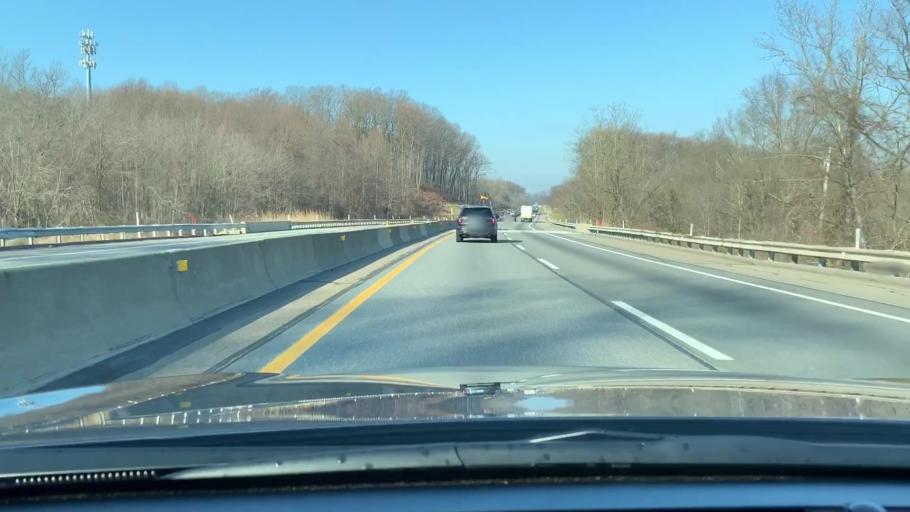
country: US
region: Pennsylvania
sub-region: Chester County
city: Elverson
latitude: 40.1033
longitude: -75.7547
